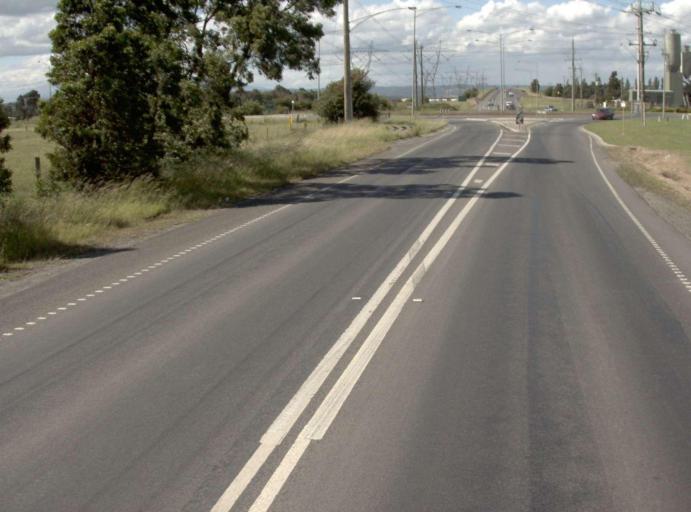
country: AU
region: Victoria
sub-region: Latrobe
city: Morwell
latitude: -38.2497
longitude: 146.4359
